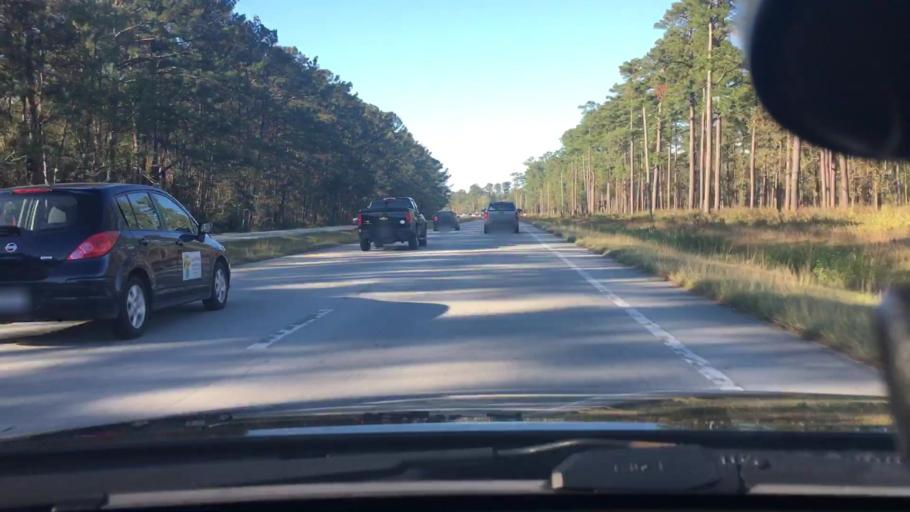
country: US
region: North Carolina
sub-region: Craven County
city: Neuse Forest
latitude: 34.9916
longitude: -76.9829
